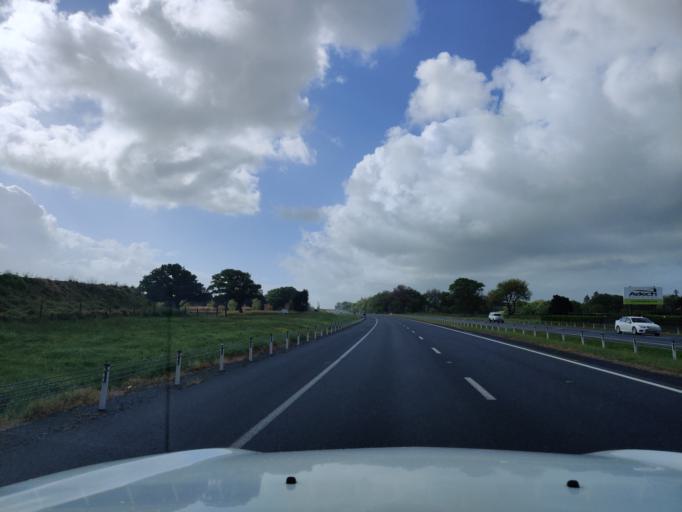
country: NZ
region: Waikato
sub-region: Waipa District
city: Cambridge
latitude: -37.8397
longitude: 175.3689
